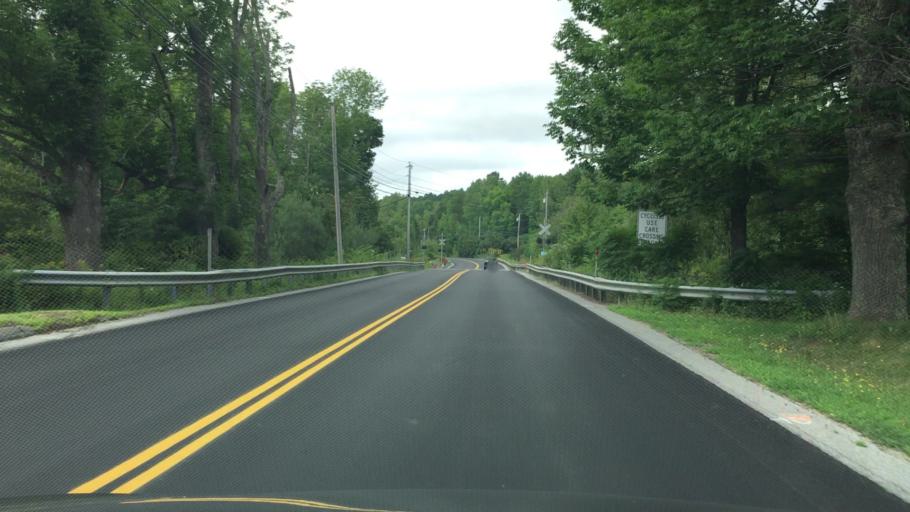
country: US
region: Maine
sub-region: Waldo County
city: Winterport
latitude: 44.6157
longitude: -68.8263
